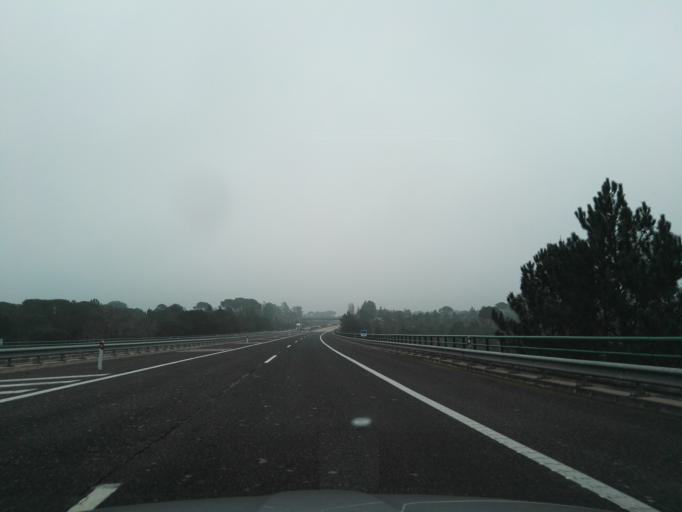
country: PT
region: Evora
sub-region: Vendas Novas
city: Vendas Novas
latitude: 38.6387
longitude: -8.4979
